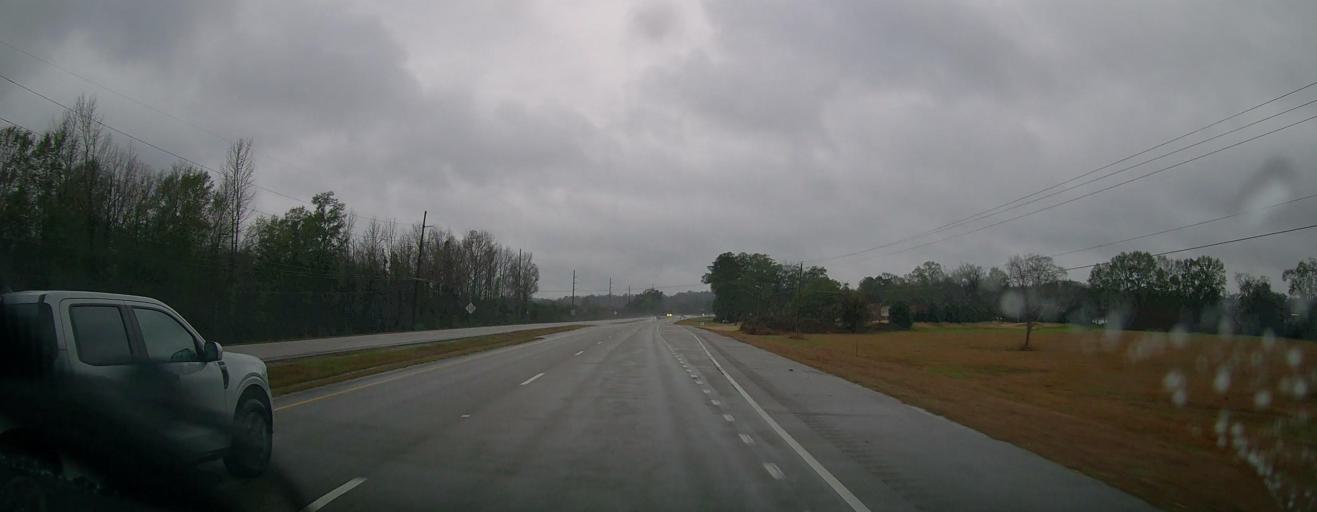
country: US
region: Alabama
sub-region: Autauga County
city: Prattville
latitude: 32.4415
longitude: -86.4794
